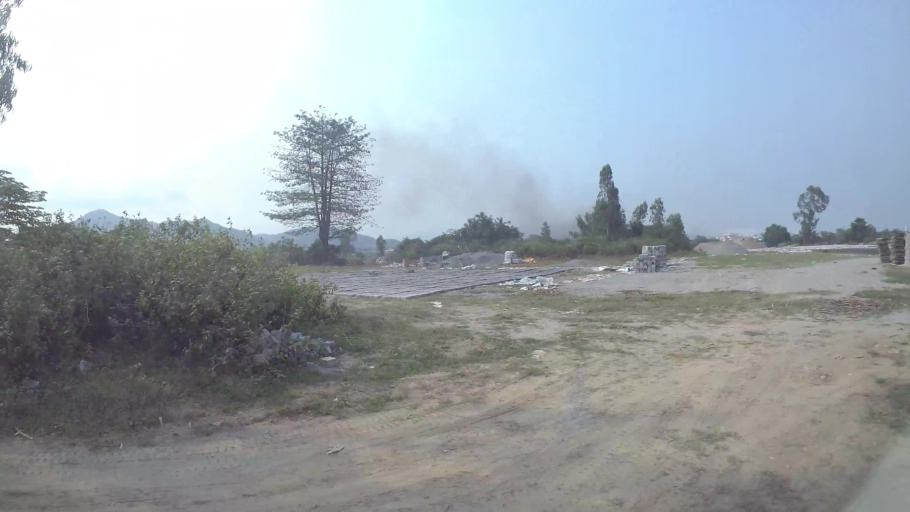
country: VN
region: Da Nang
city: Lien Chieu
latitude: 16.0423
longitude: 108.1605
